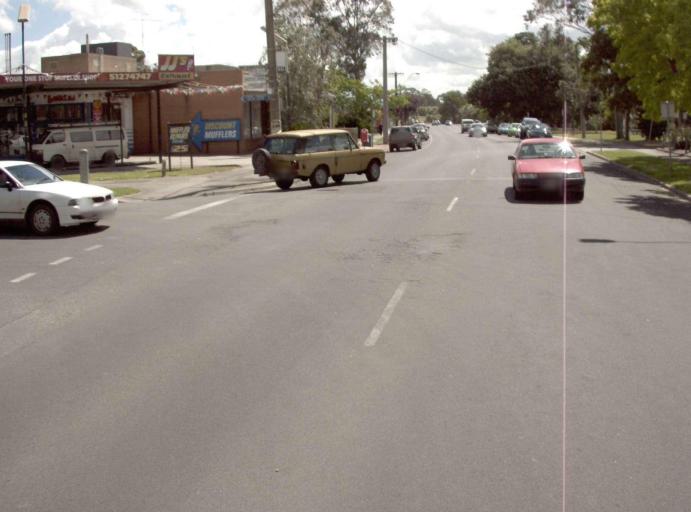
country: AU
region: Victoria
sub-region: Latrobe
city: Moe
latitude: -38.1772
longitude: 146.2613
